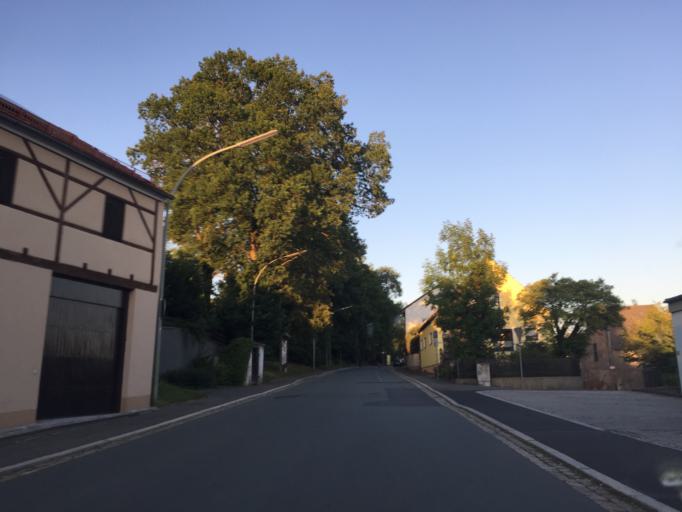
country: DE
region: Bavaria
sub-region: Upper Palatinate
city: Pressath
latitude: 49.7680
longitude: 11.9359
